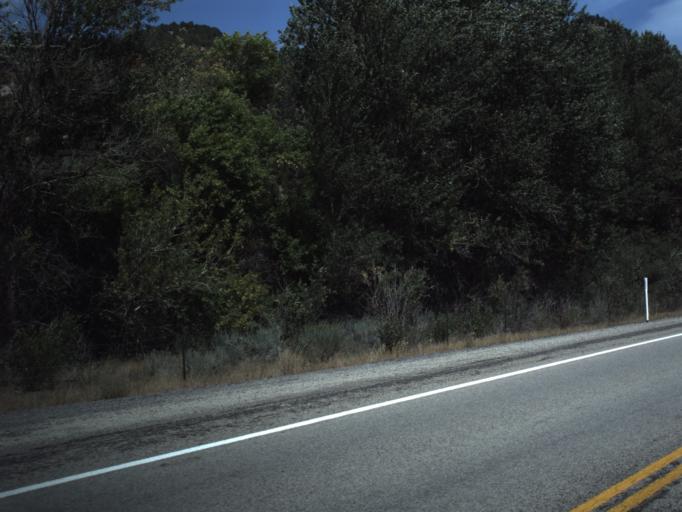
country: US
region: Utah
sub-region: Utah County
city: Woodland Hills
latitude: 39.9585
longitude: -111.5280
